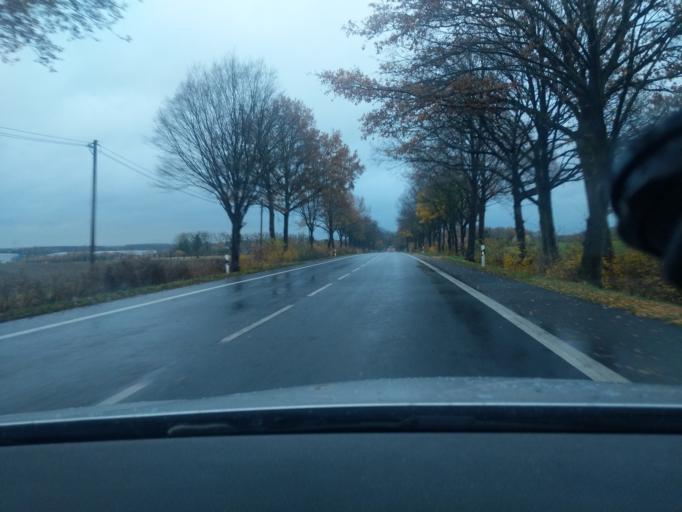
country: DE
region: North Rhine-Westphalia
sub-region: Regierungsbezirk Arnsberg
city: Bonen
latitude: 51.6070
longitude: 7.7999
